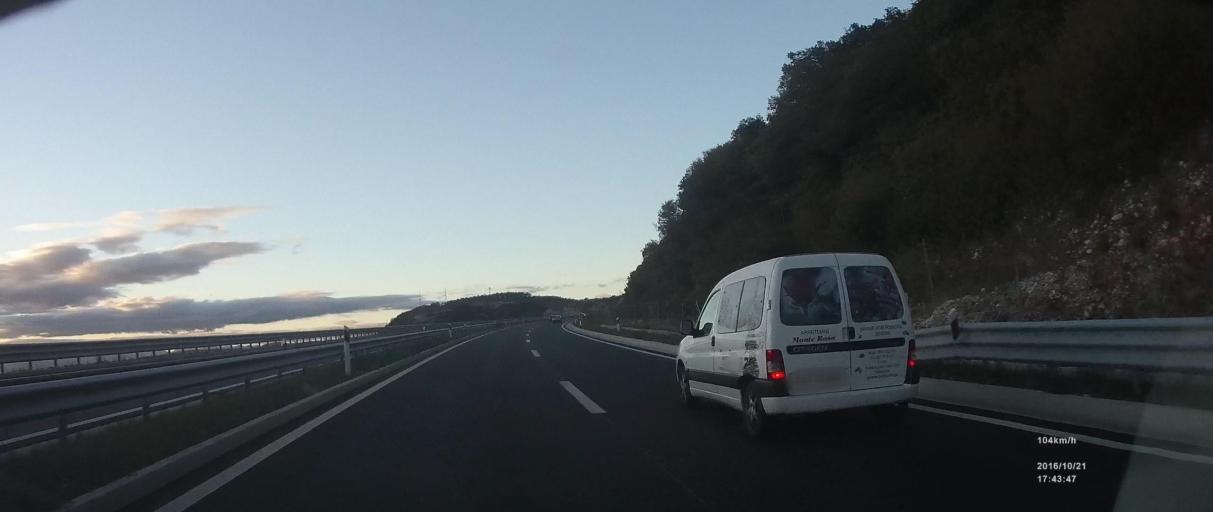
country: HR
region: Primorsko-Goranska
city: Hreljin
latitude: 45.2716
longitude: 14.6018
